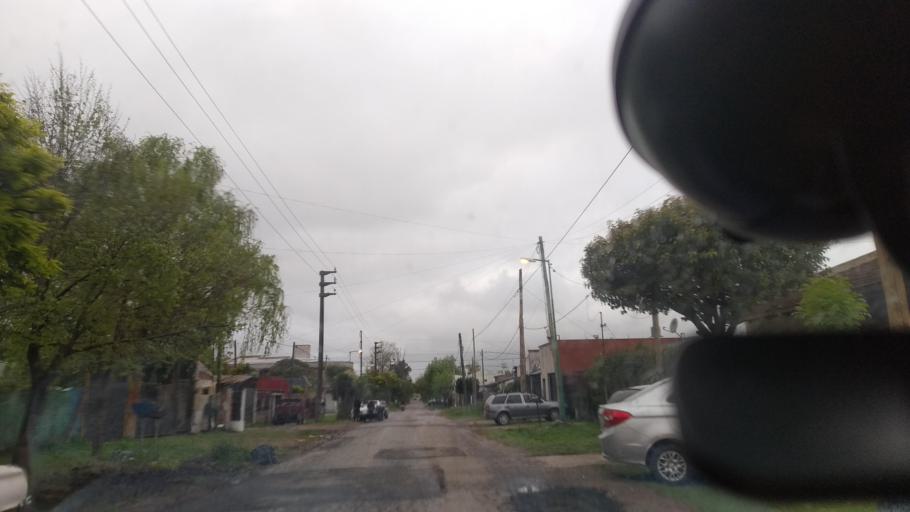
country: AR
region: Buenos Aires
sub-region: Partido de La Plata
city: La Plata
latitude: -34.9535
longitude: -57.9939
